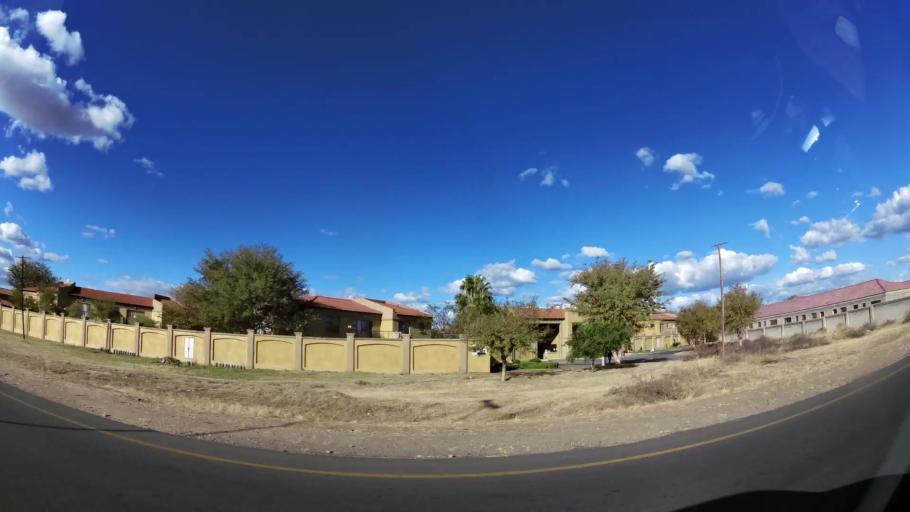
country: ZA
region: Limpopo
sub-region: Capricorn District Municipality
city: Polokwane
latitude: -23.9344
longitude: 29.4493
